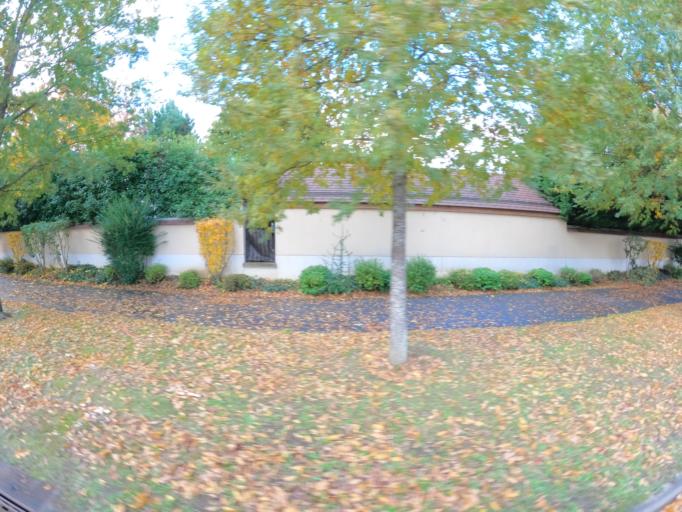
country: FR
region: Ile-de-France
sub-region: Departement de Seine-et-Marne
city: Magny-le-Hongre
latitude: 48.8742
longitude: 2.8147
